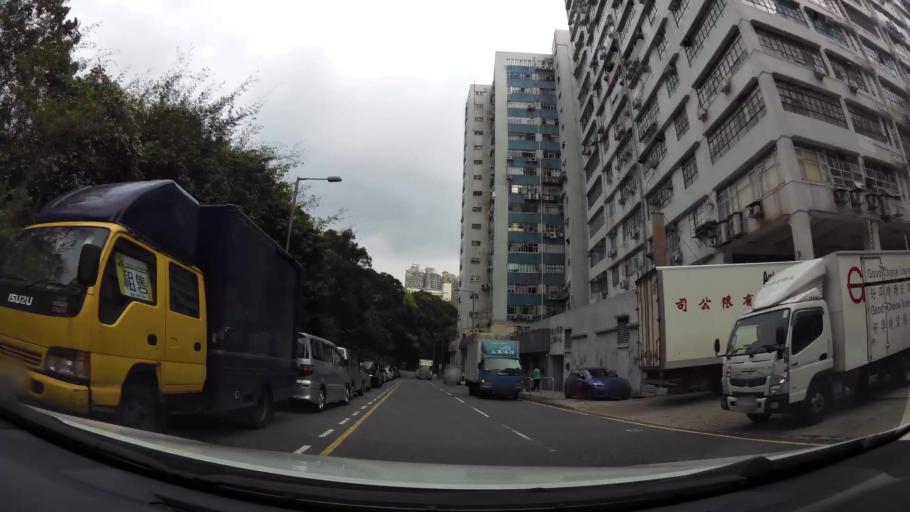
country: HK
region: Sha Tin
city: Sha Tin
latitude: 22.4000
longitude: 114.1942
